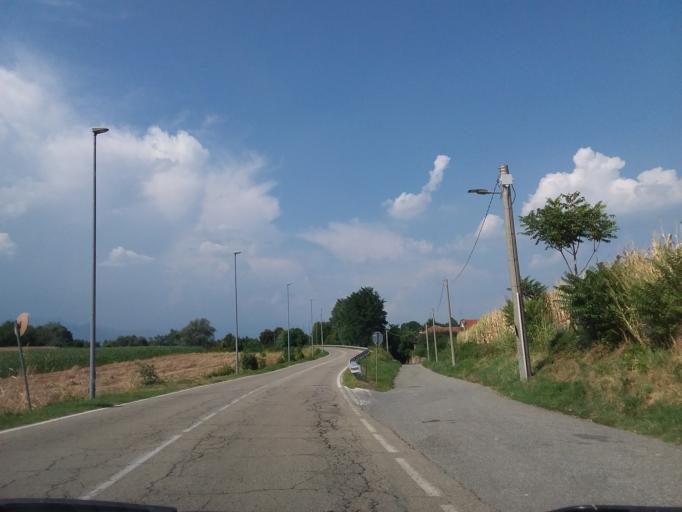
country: IT
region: Piedmont
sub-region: Provincia di Torino
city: Rivoli
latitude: 45.0784
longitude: 7.5423
